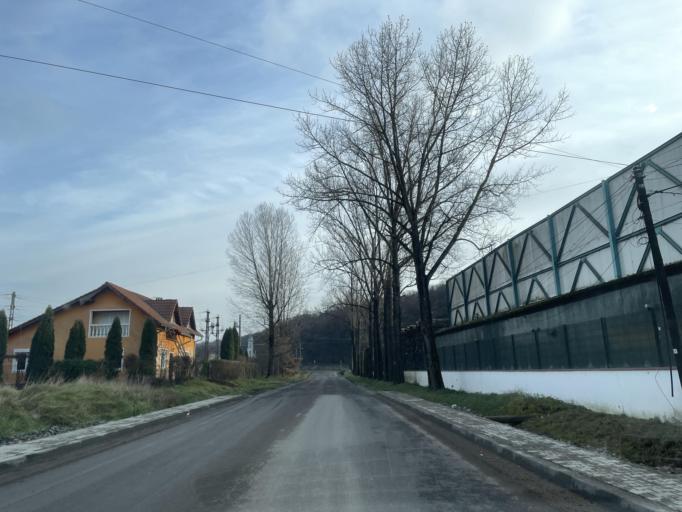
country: RO
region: Mures
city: Reghin-Sat
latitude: 46.7774
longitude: 24.7386
